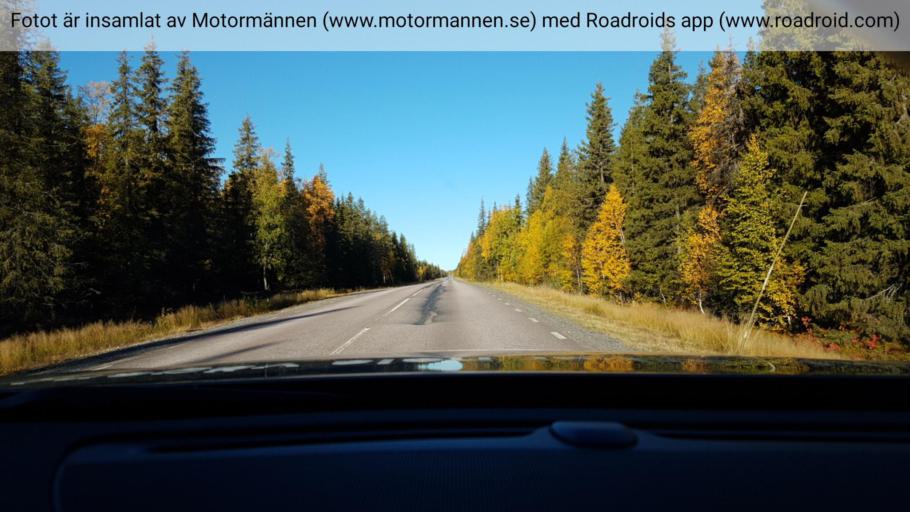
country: SE
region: Vaesterbotten
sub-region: Skelleftea Kommun
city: Storvik
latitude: 65.3538
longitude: 20.4786
